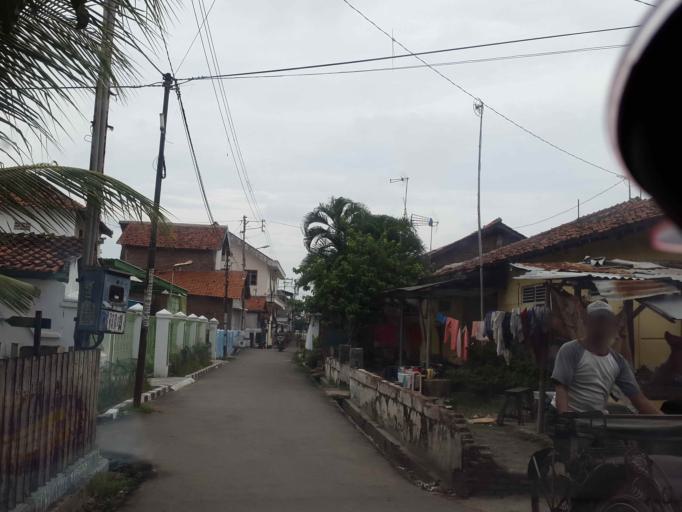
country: ID
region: Central Java
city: Tegal
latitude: -6.8700
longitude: 109.1227
